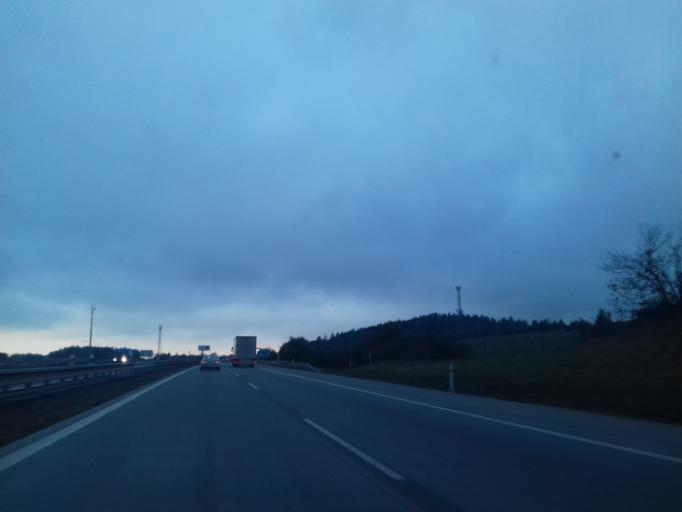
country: CZ
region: Vysocina
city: Krizanov
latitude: 49.3065
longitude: 16.1241
